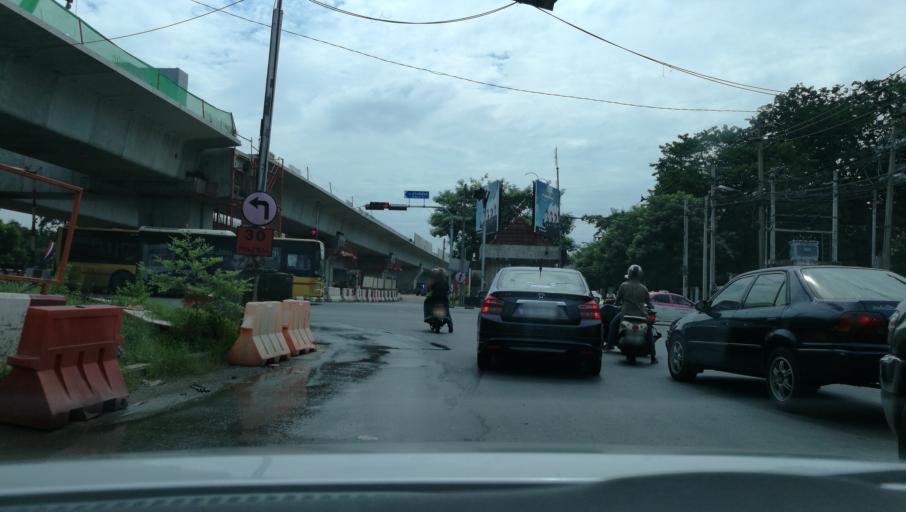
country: TH
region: Bangkok
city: Phaya Thai
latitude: 13.7928
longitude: 100.5350
